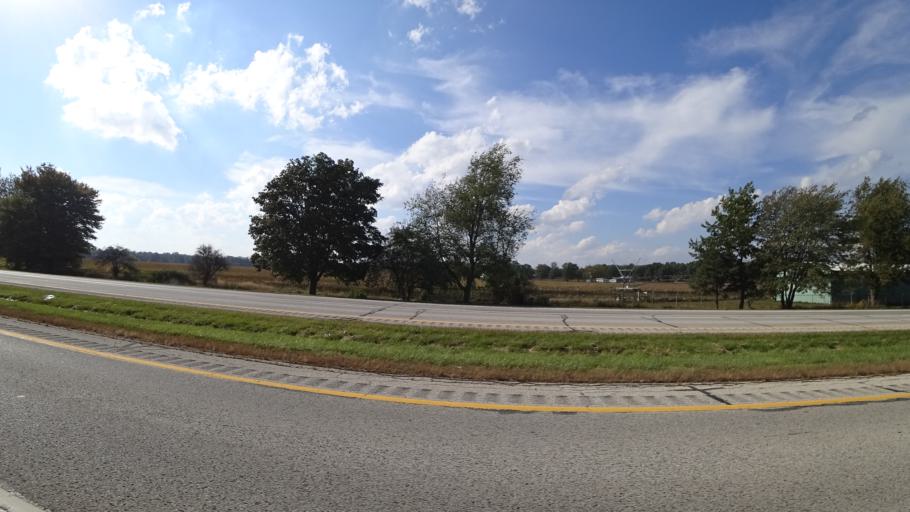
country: US
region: Michigan
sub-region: Saint Joseph County
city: Three Rivers
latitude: 41.9671
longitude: -85.6383
